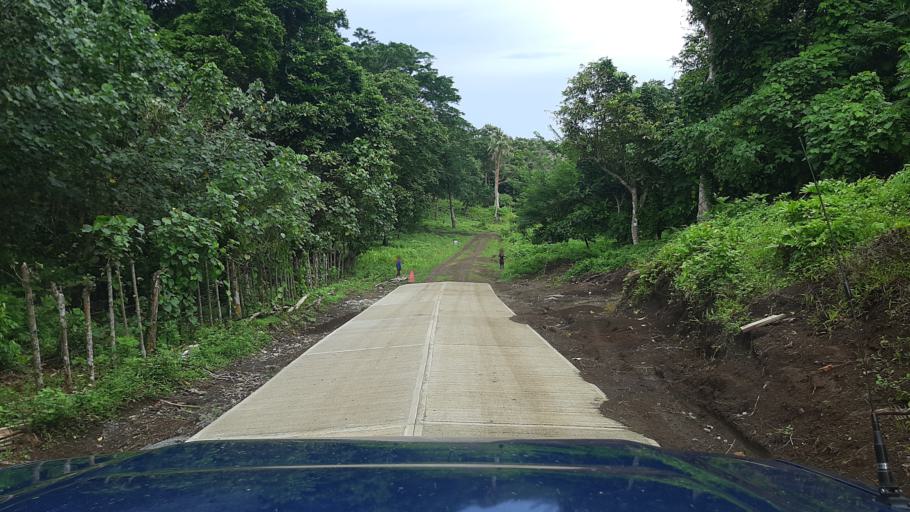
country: VU
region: Shefa
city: Port-Vila
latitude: -16.8999
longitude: 168.5739
